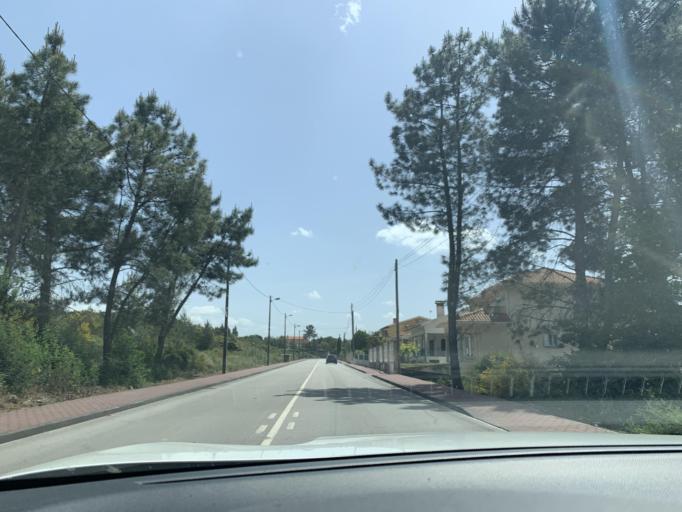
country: PT
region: Viseu
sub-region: Mangualde
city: Mangualde
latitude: 40.6109
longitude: -7.7472
